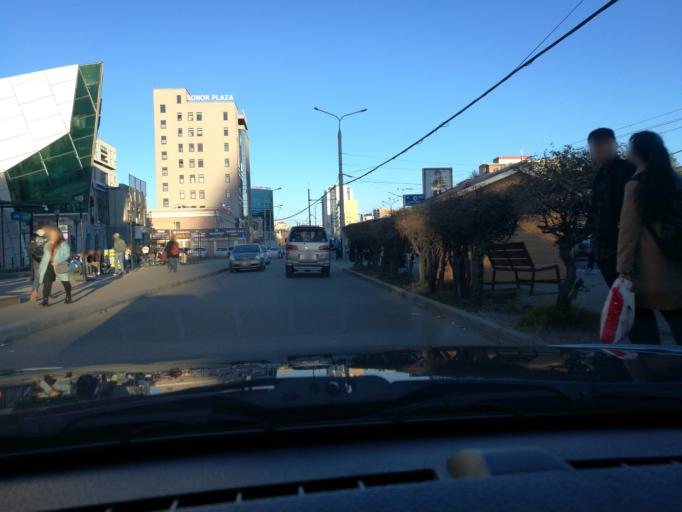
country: MN
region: Ulaanbaatar
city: Ulaanbaatar
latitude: 47.9182
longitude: 106.9254
